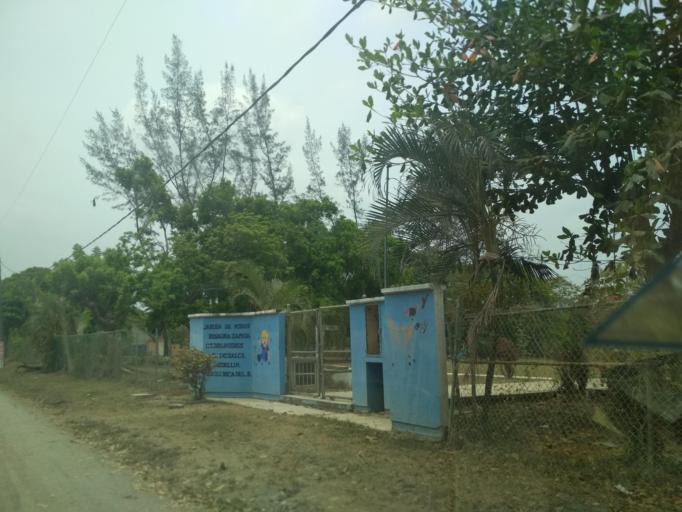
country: MX
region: Veracruz
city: El Tejar
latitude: 19.0434
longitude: -96.1702
